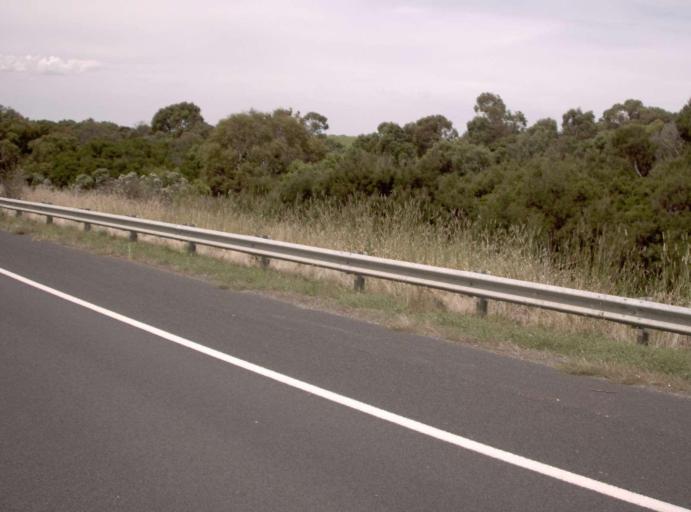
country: AU
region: Victoria
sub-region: Mornington Peninsula
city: Mount Martha
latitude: -38.2854
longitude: 145.0509
